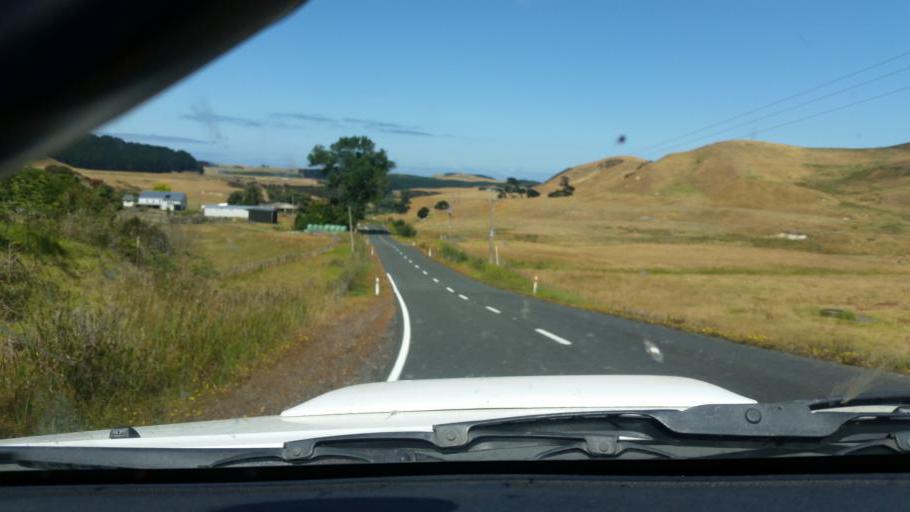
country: NZ
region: Northland
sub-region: Kaipara District
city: Dargaville
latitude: -35.8217
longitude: 173.6831
